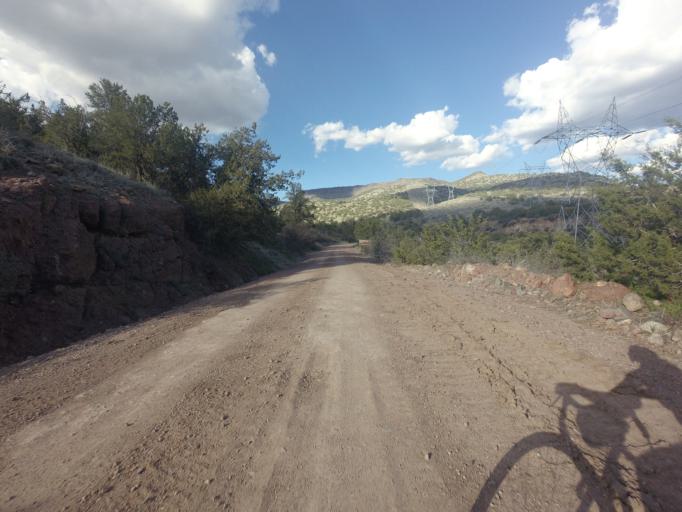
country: US
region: Arizona
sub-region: Gila County
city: Pine
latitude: 34.3939
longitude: -111.6514
